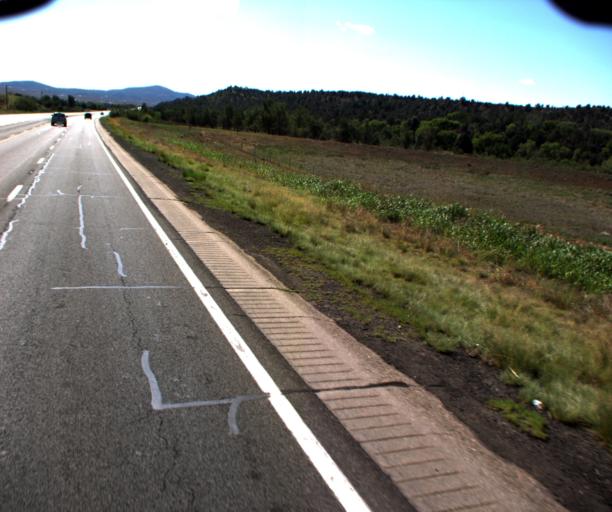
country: US
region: Arizona
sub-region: Yavapai County
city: Prescott Valley
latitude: 34.5723
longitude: -112.2774
